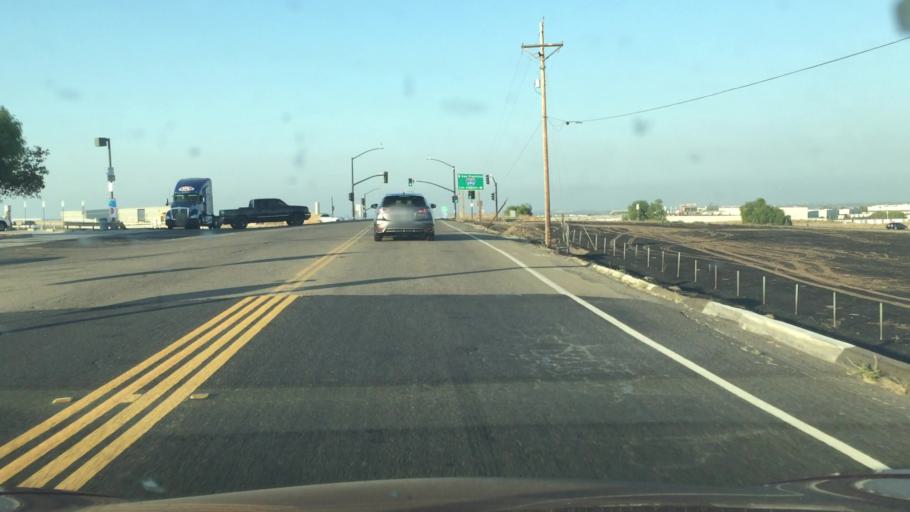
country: US
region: California
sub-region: San Joaquin County
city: Mountain House
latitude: 37.7187
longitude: -121.5372
